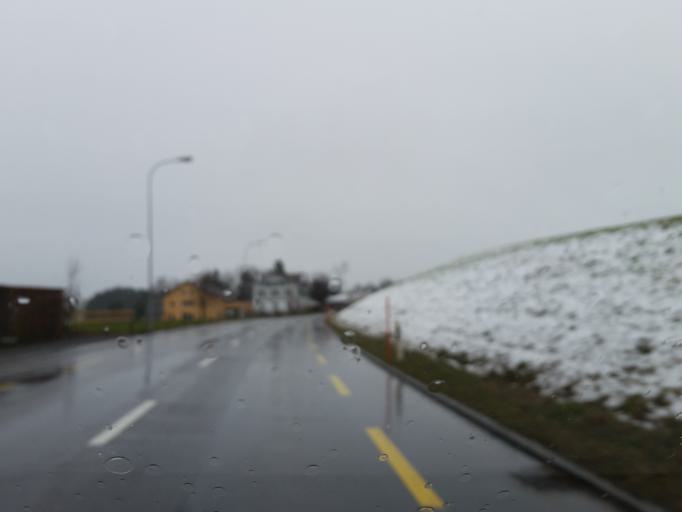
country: CH
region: Appenzell Innerrhoden
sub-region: Appenzell Inner Rhodes
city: Gonten
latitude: 47.3691
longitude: 9.3297
